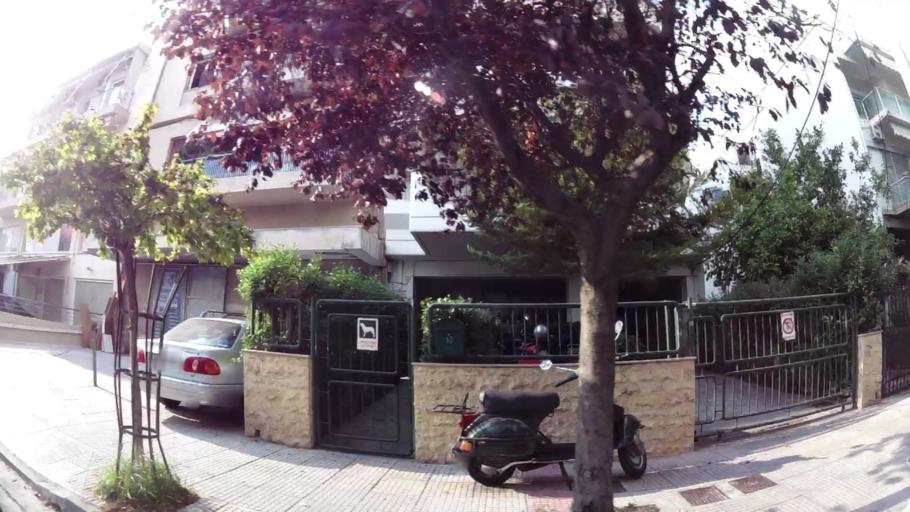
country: GR
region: Attica
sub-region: Nomarchia Athinas
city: Moskhaton
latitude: 37.9468
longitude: 23.6895
